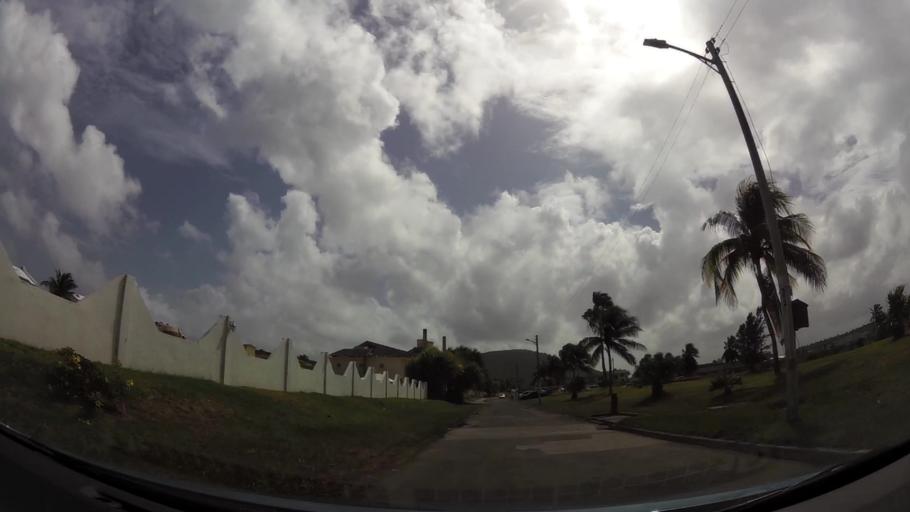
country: KN
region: Saint Peter Basseterre
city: Monkey Hill
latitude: 17.2947
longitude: -62.6865
